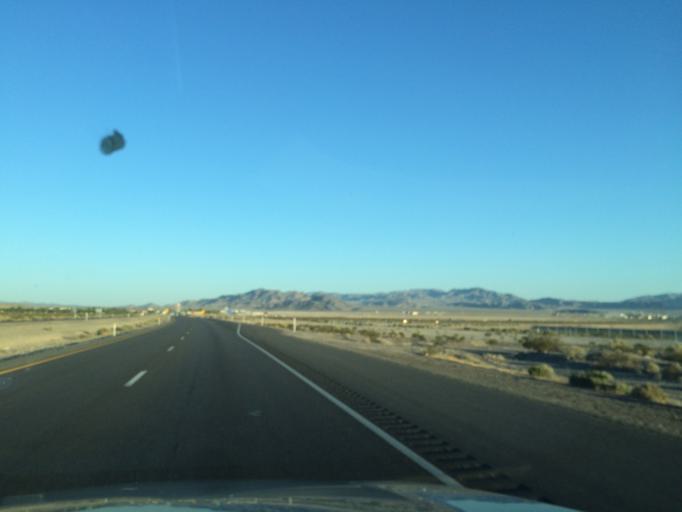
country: US
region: Nevada
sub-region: Nye County
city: Pahrump
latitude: 36.5766
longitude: -115.6457
